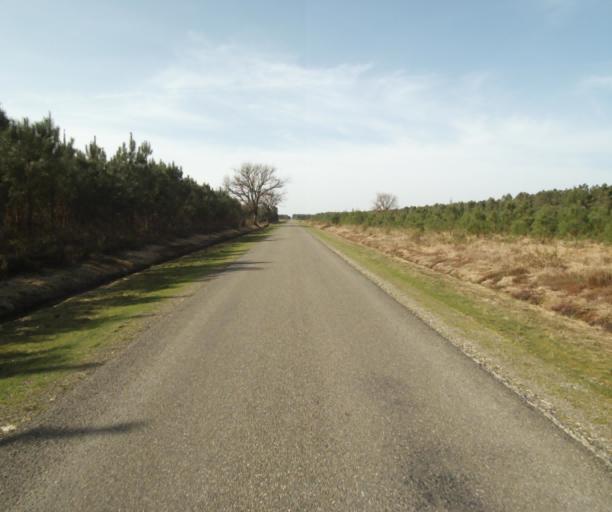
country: FR
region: Aquitaine
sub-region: Departement des Landes
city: Roquefort
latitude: 44.1776
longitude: -0.2004
